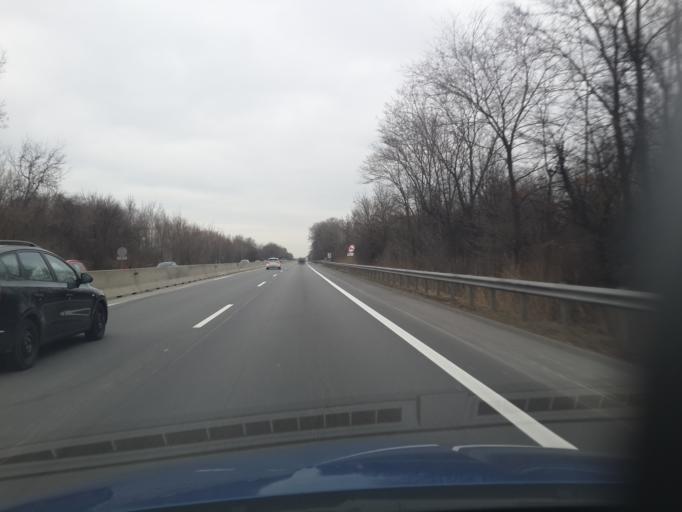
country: AT
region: Lower Austria
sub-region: Politischer Bezirk Bruck an der Leitha
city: Bruck an der Leitha
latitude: 48.0492
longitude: 16.7370
